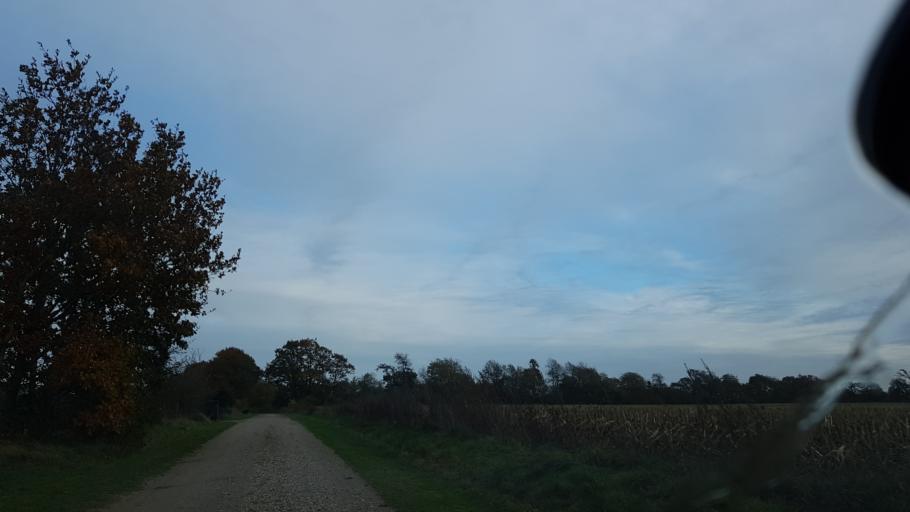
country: DK
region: South Denmark
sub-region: Haderslev Kommune
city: Vojens
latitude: 55.2918
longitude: 9.2228
